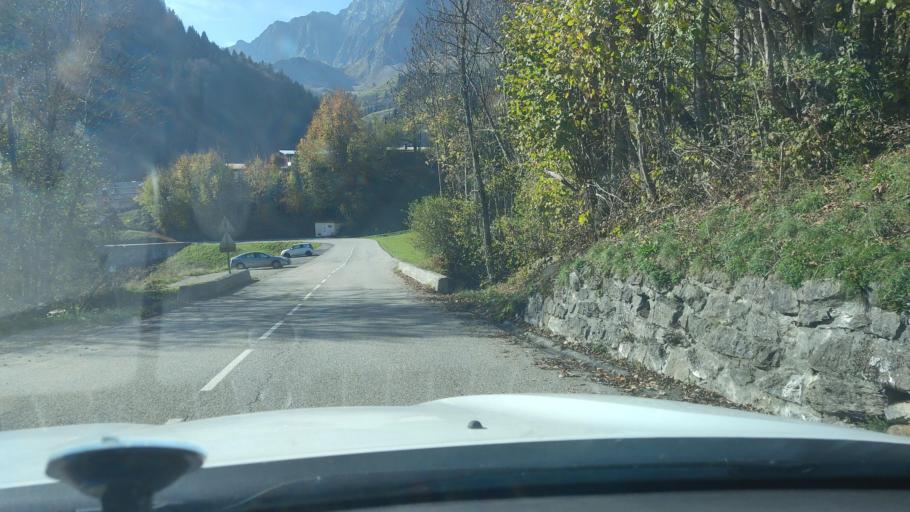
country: FR
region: Rhone-Alpes
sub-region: Departement de la Haute-Savoie
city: La Clusaz
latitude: 45.8666
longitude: 6.4958
